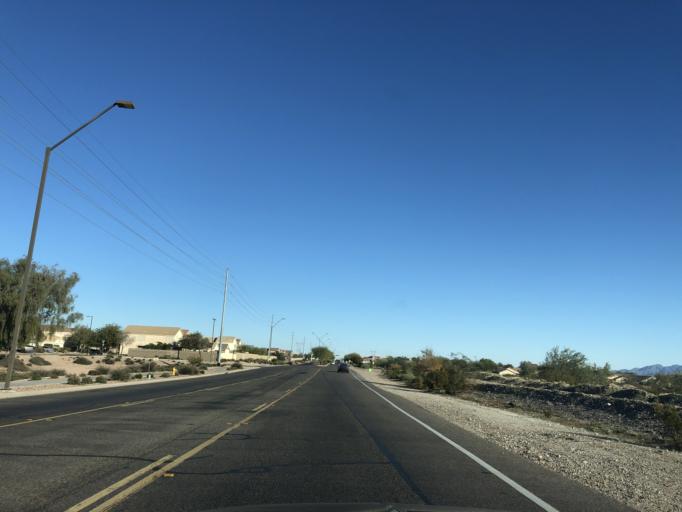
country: US
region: Arizona
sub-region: Maricopa County
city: Buckeye
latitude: 33.4356
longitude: -112.5674
